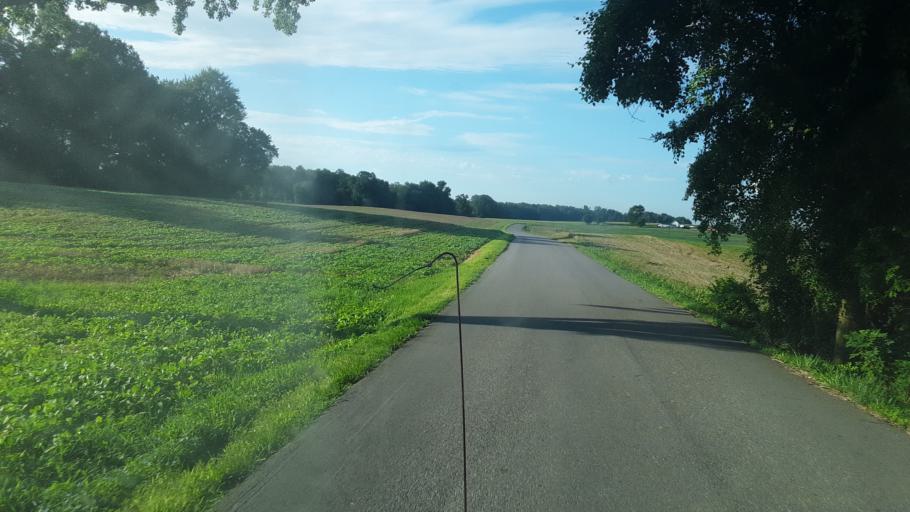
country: US
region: Kentucky
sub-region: Todd County
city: Guthrie
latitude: 36.7121
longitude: -87.1714
